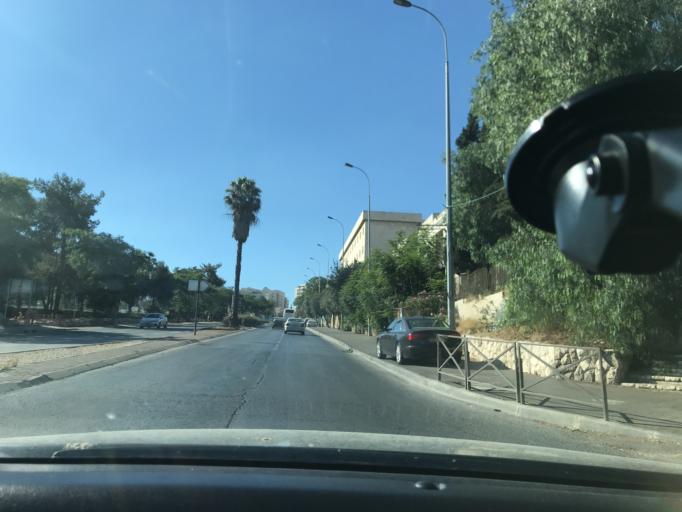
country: IL
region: Jerusalem
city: West Jerusalem
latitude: 31.7839
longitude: 35.2083
